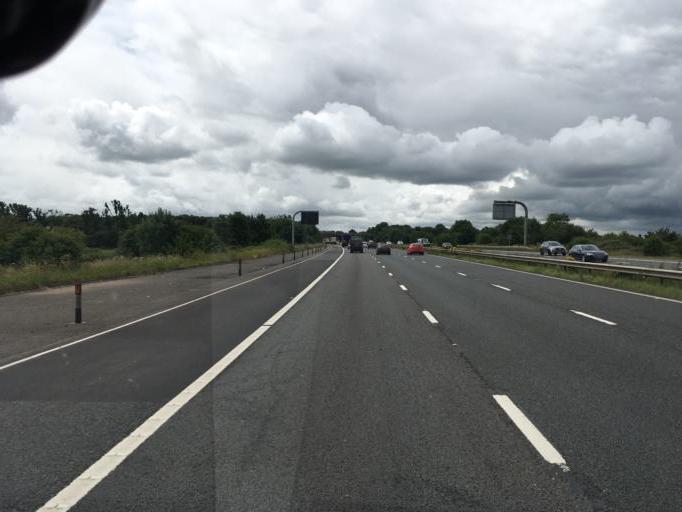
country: GB
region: England
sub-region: Gloucestershire
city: Stonehouse
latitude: 51.7820
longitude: -2.3053
